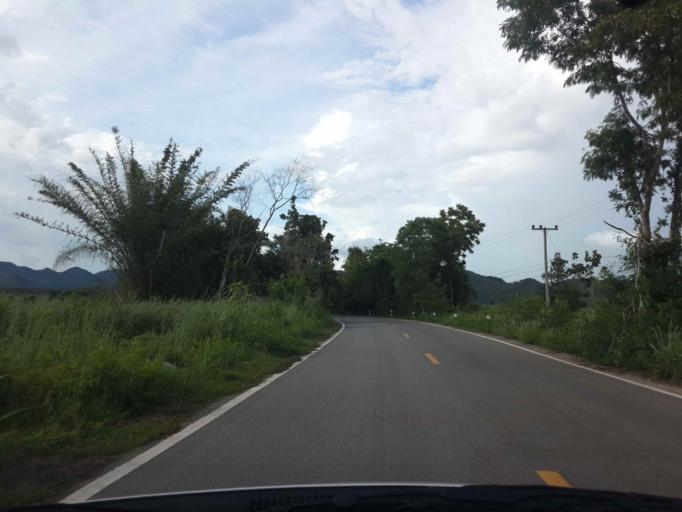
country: TH
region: Kanchanaburi
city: Dan Makham Tia
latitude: 13.8607
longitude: 99.1668
